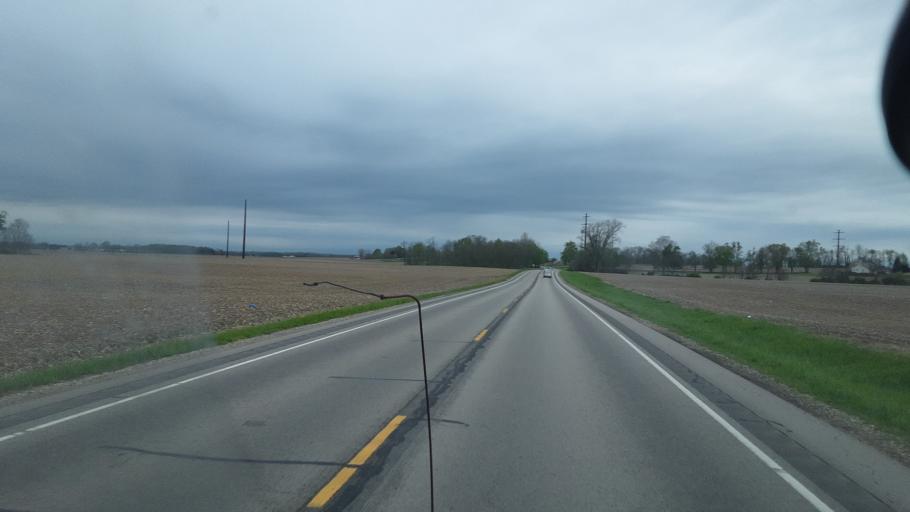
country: US
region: Indiana
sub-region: Kosciusko County
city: Syracuse
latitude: 41.4776
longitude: -85.7037
